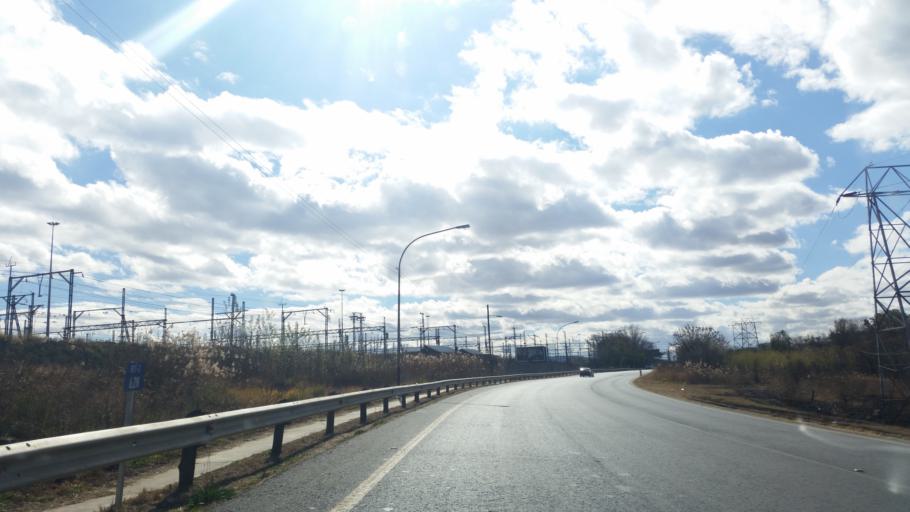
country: ZA
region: KwaZulu-Natal
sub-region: uThukela District Municipality
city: Ladysmith
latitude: -28.5449
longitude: 29.7941
